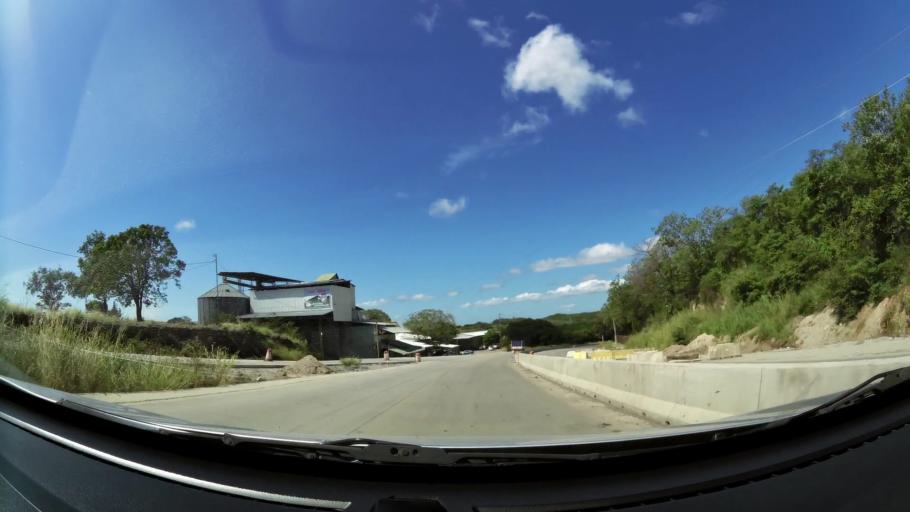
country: CR
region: Guanacaste
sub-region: Canton de Canas
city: Canas
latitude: 10.4327
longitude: -85.1022
